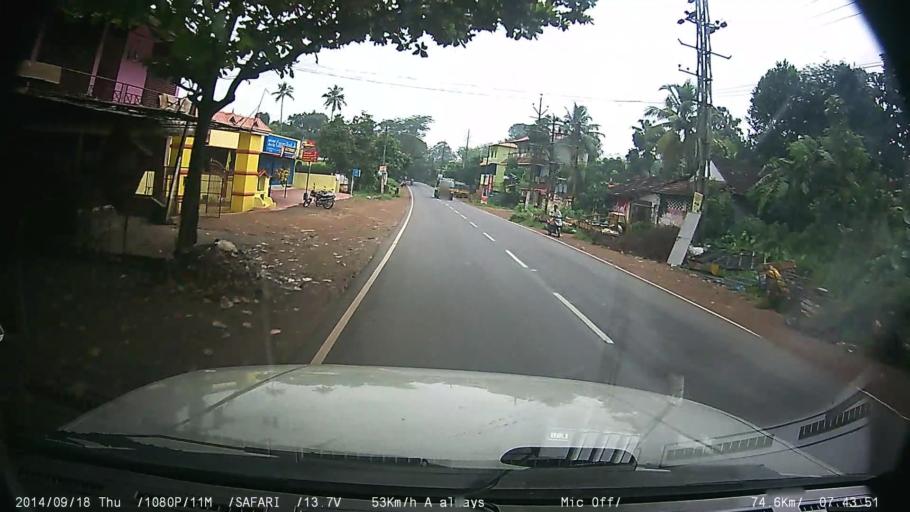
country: IN
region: Kerala
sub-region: Kottayam
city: Changanacheri
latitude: 9.4766
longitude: 76.5763
